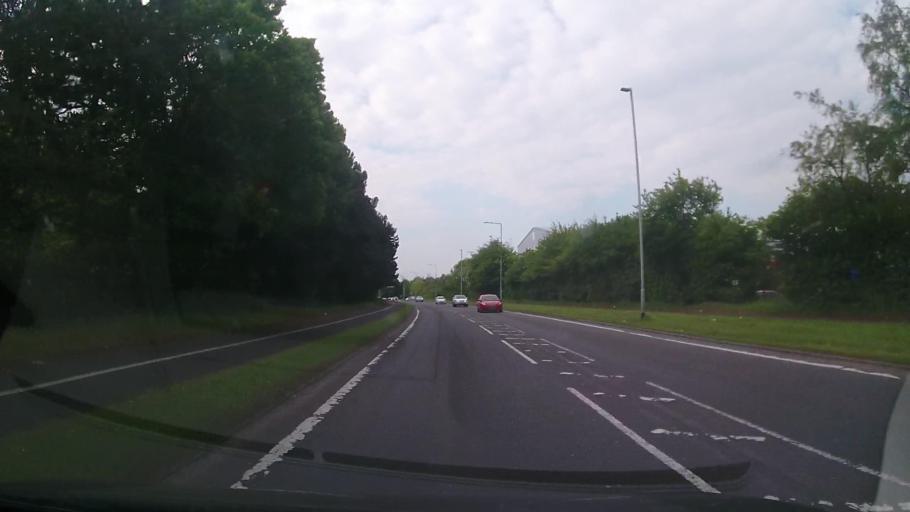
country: GB
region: England
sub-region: Shropshire
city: Hadley
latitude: 52.7153
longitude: -2.4718
